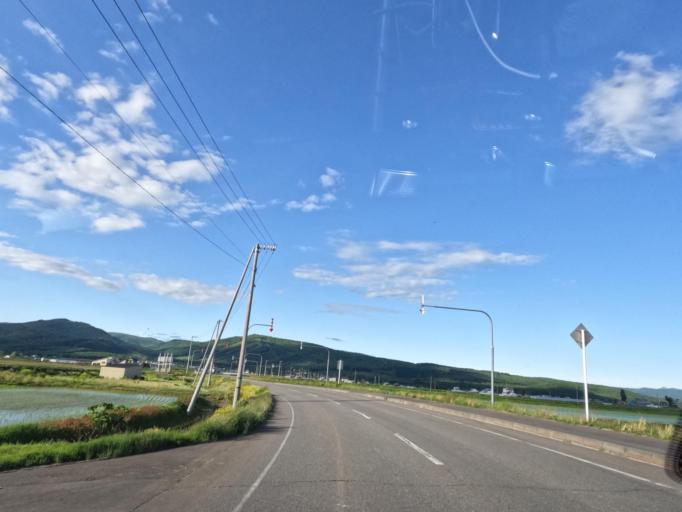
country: JP
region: Hokkaido
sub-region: Asahikawa-shi
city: Asahikawa
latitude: 43.8983
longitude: 142.4769
